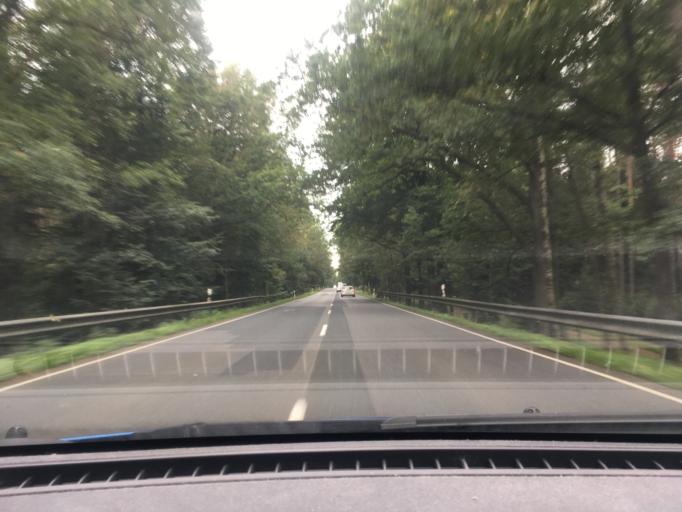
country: DE
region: Lower Saxony
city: Unterluss
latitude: 52.7751
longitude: 10.3285
